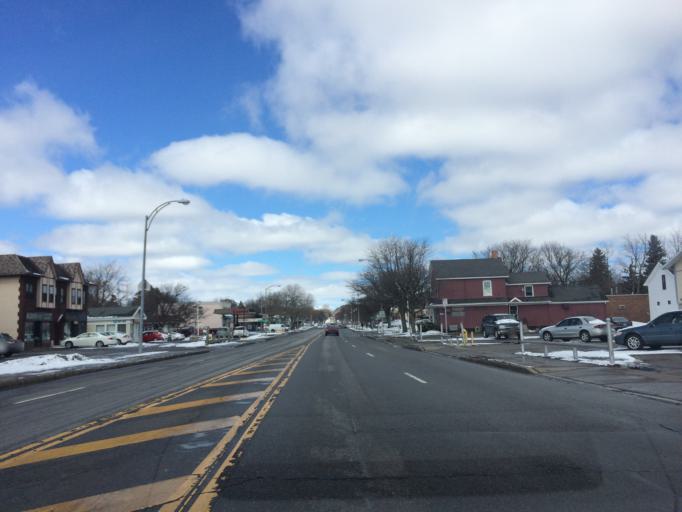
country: US
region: New York
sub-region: Monroe County
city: Brighton
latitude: 43.1276
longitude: -77.5658
